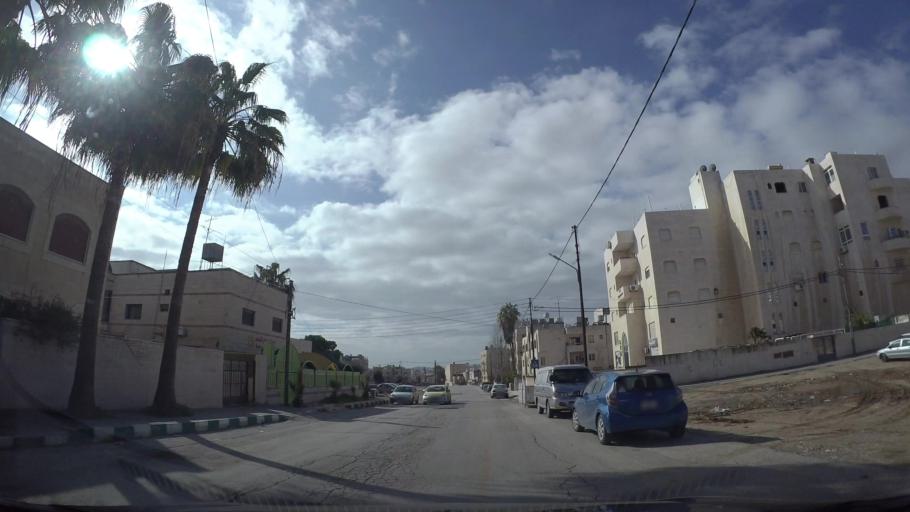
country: JO
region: Amman
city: Wadi as Sir
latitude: 31.9521
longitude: 35.8413
